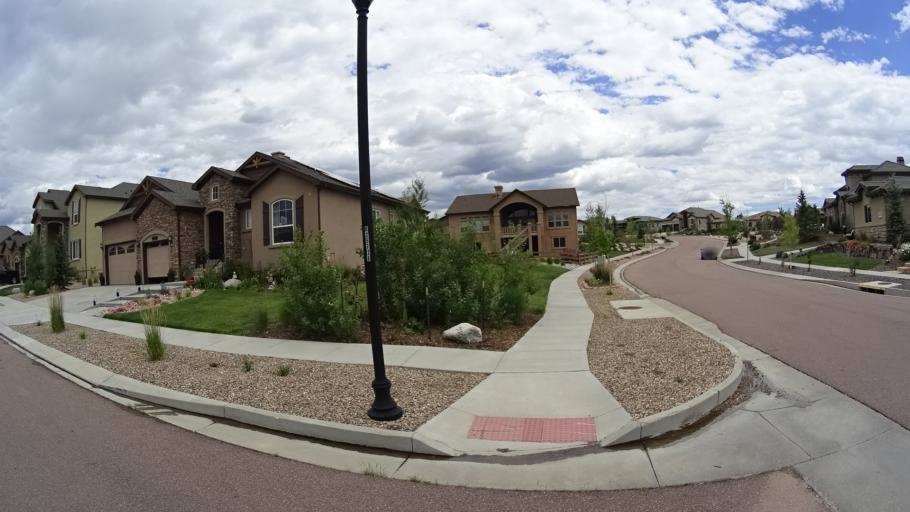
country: US
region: Colorado
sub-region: El Paso County
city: Gleneagle
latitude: 39.0208
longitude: -104.8025
